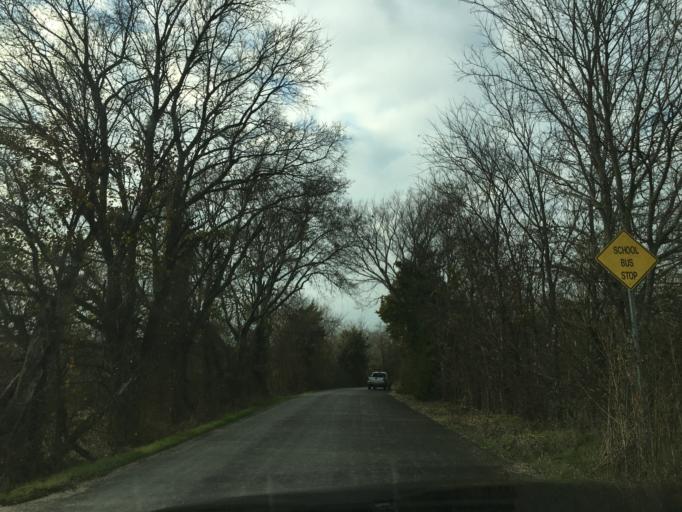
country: US
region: Texas
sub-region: Ellis County
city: Red Oak
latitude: 32.4850
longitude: -96.7949
